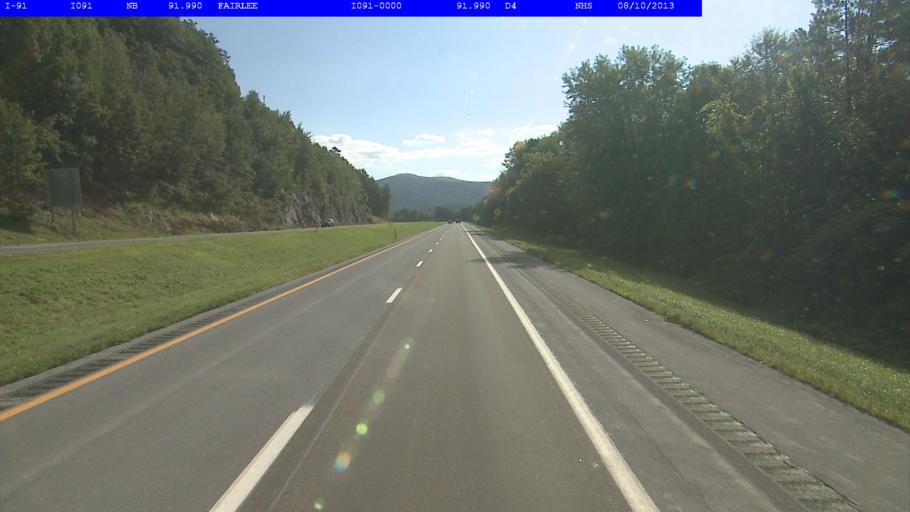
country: US
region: New Hampshire
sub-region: Grafton County
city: Orford
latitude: 43.9090
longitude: -72.1447
